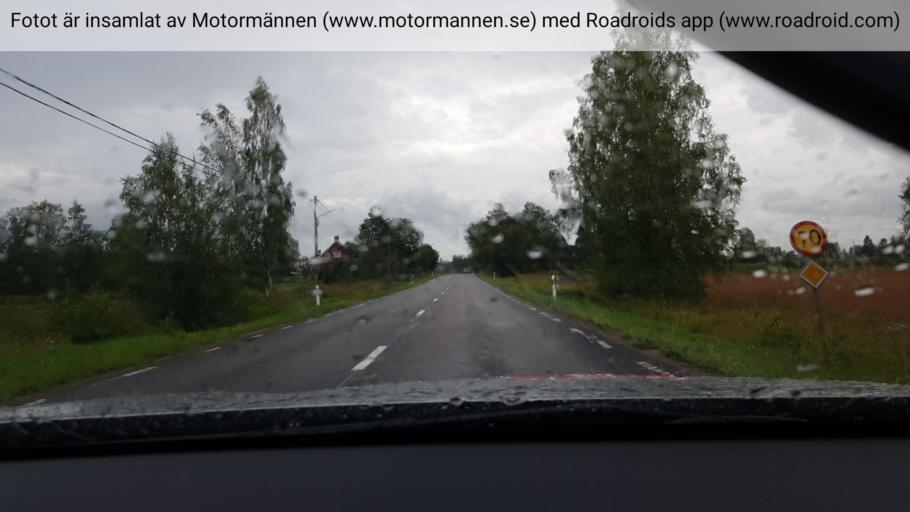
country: SE
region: Uppsala
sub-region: Tierps Kommun
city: Karlholmsbruk
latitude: 60.5080
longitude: 17.6573
